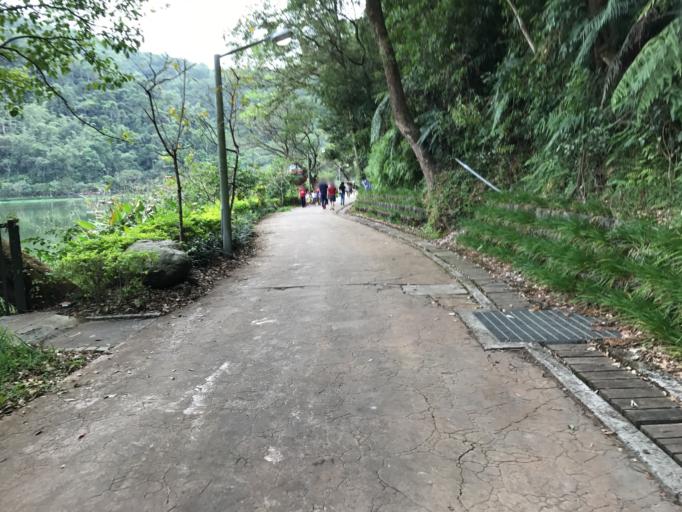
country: TW
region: Taiwan
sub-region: Nantou
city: Puli
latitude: 23.9609
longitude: 120.9969
